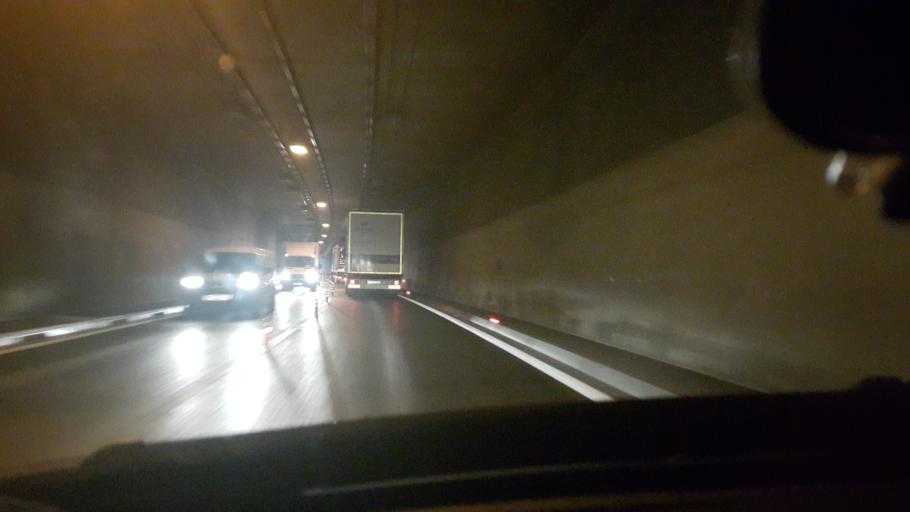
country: AT
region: Carinthia
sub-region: Politischer Bezirk Klagenfurt Land
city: Poggersdorf
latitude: 46.6465
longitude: 14.5059
